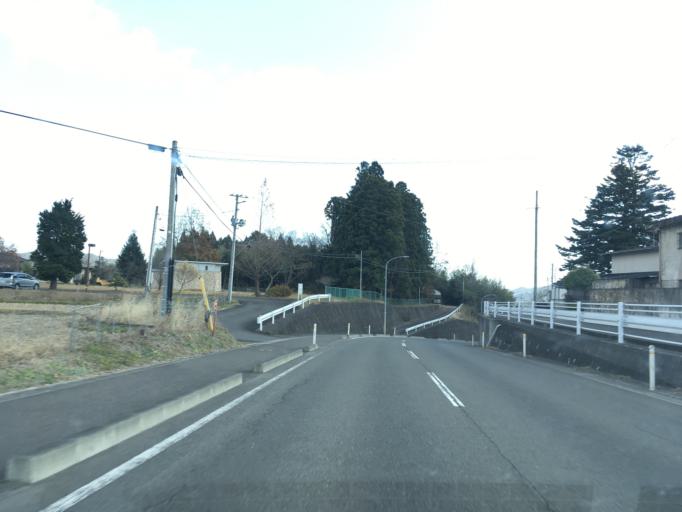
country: JP
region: Miyagi
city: Sendai
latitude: 38.2809
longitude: 140.7582
